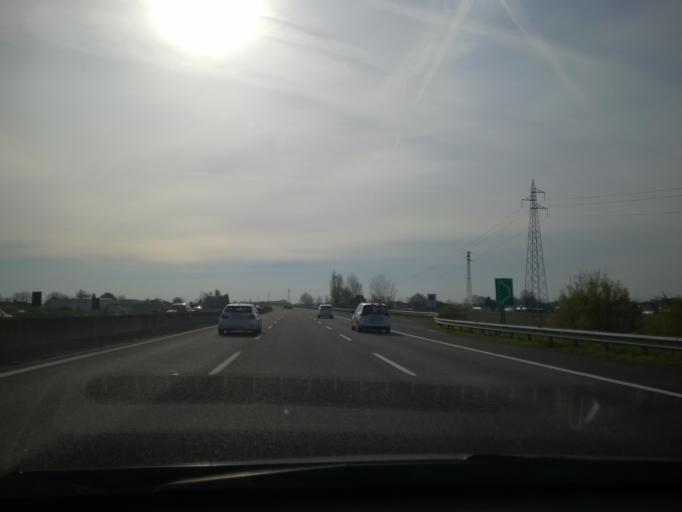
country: IT
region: Emilia-Romagna
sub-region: Forli-Cesena
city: Forli
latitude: 44.2848
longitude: 12.0025
